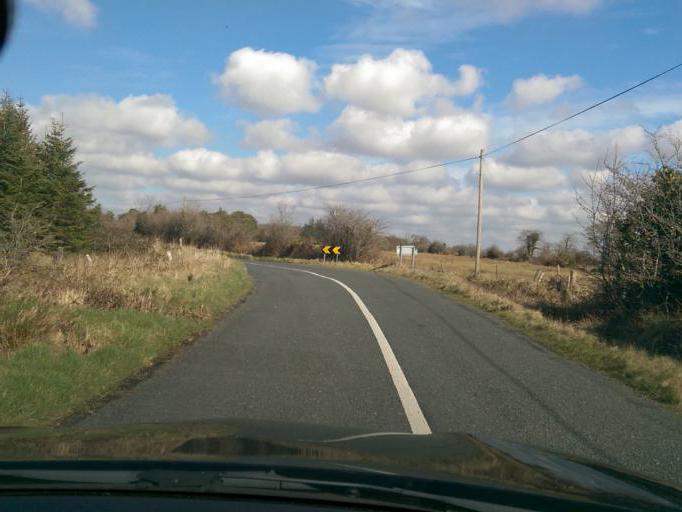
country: IE
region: Connaught
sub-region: County Galway
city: Athenry
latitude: 53.4529
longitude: -8.5505
